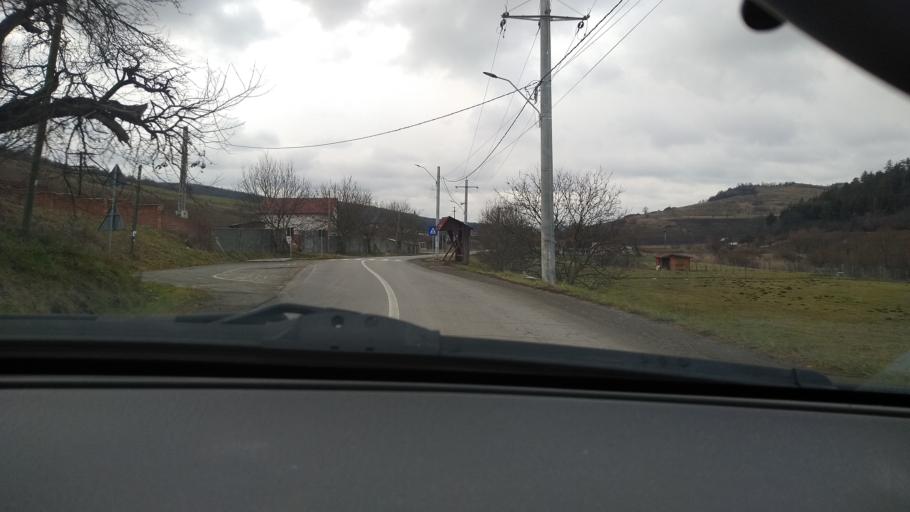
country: RO
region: Mures
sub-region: Comuna Pasareni
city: Pasareni
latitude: 46.5418
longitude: 24.6931
